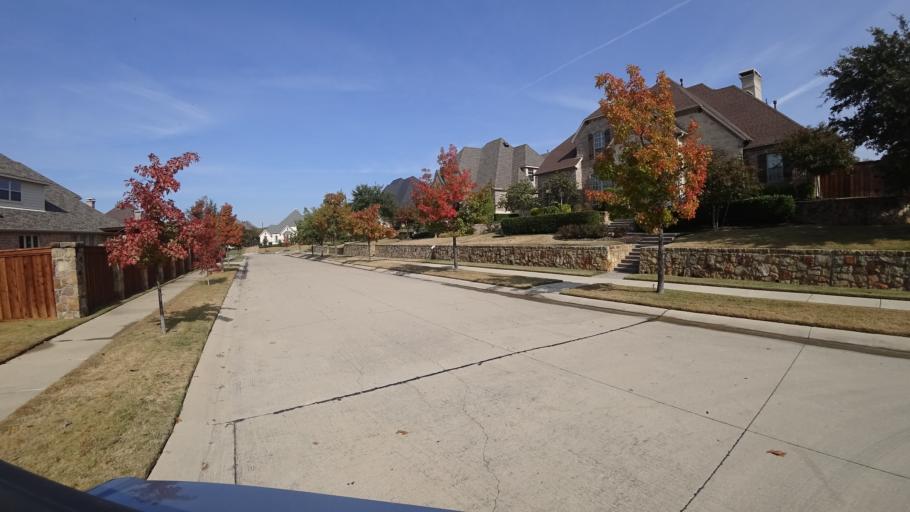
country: US
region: Texas
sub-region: Denton County
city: The Colony
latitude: 33.0415
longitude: -96.8878
